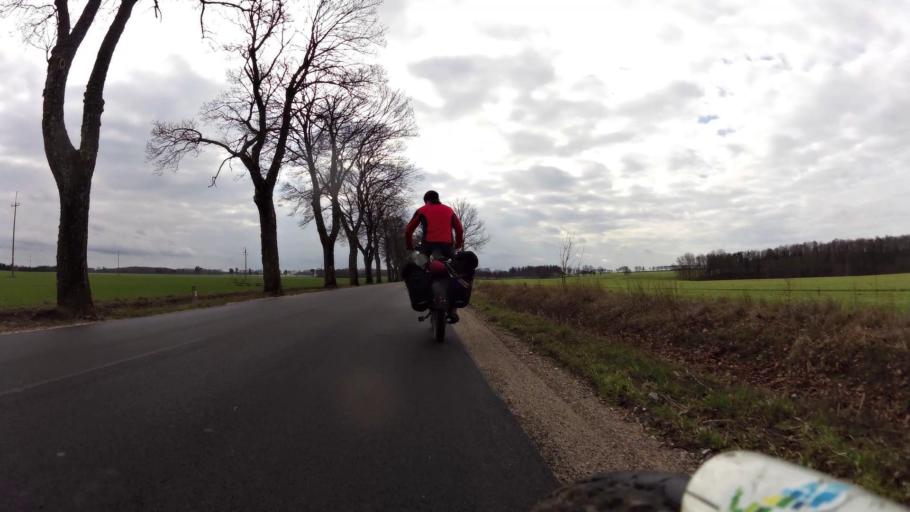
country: PL
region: Pomeranian Voivodeship
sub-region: Powiat bytowski
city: Kolczyglowy
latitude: 54.2325
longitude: 17.2422
